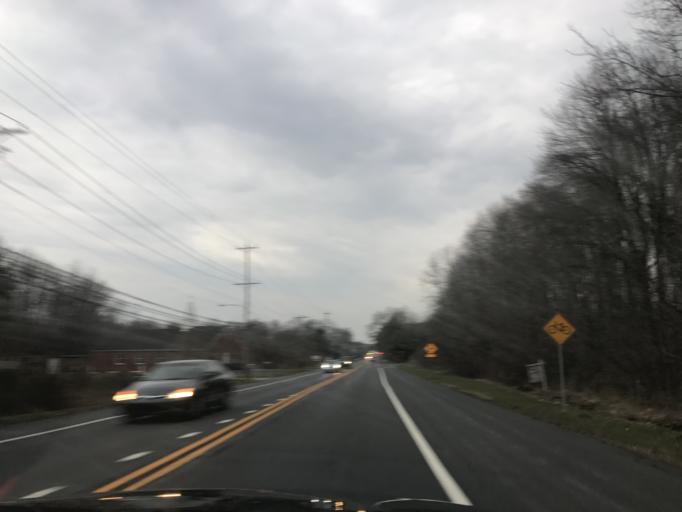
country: US
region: Delaware
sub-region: New Castle County
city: Glasgow
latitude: 39.6286
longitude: -75.7648
